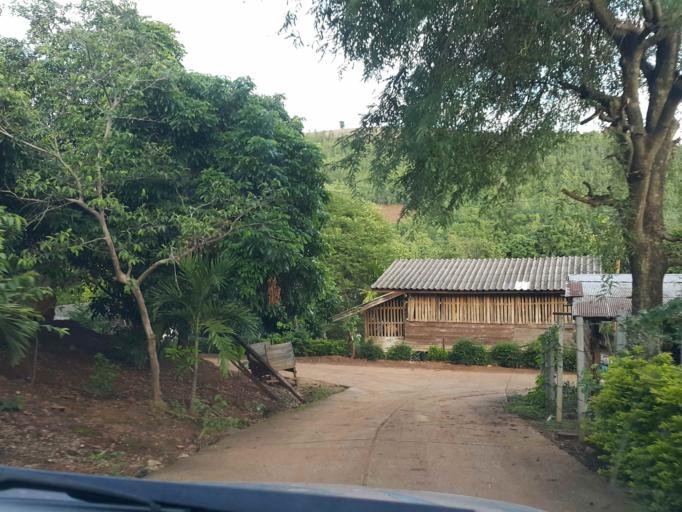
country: TH
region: Chiang Mai
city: Mae Chaem
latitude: 18.4970
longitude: 98.3970
